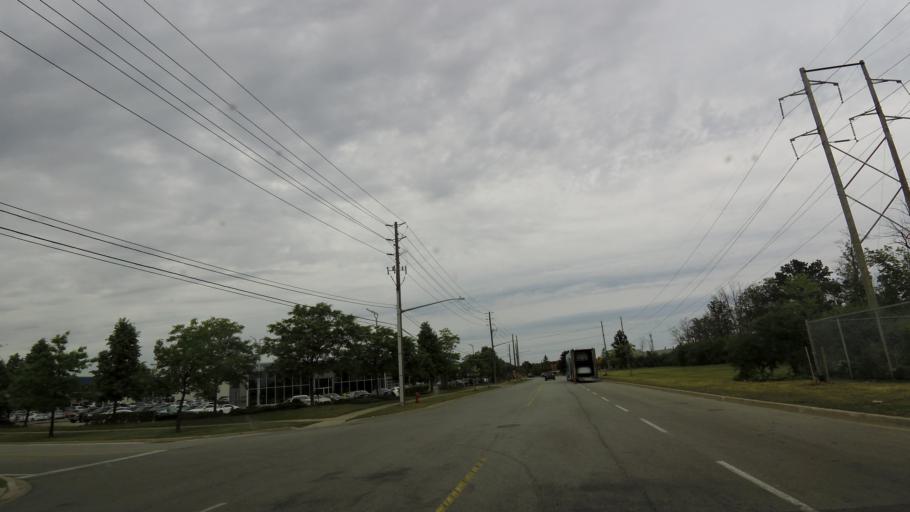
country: CA
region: Ontario
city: Oakville
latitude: 43.4081
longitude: -79.7347
